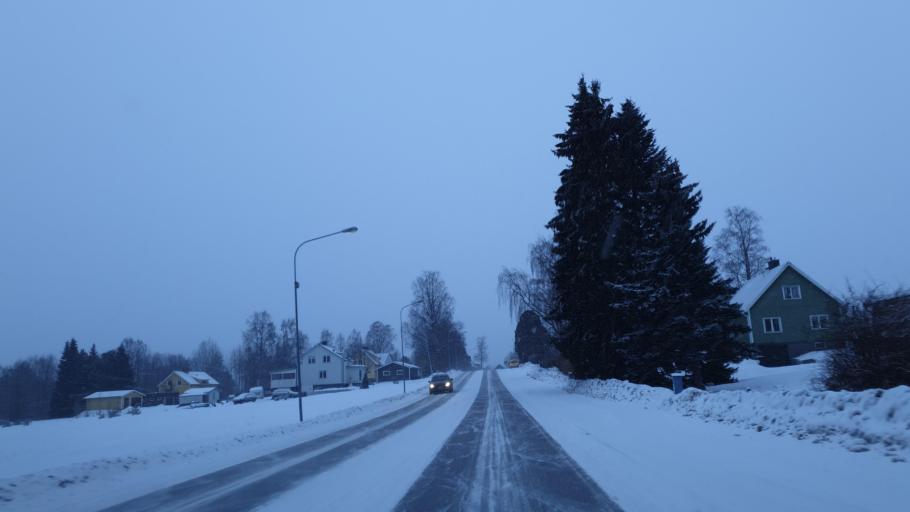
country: SE
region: Vaesternorrland
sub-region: OErnskoeldsviks Kommun
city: Ornskoldsvik
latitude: 63.2987
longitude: 18.6320
